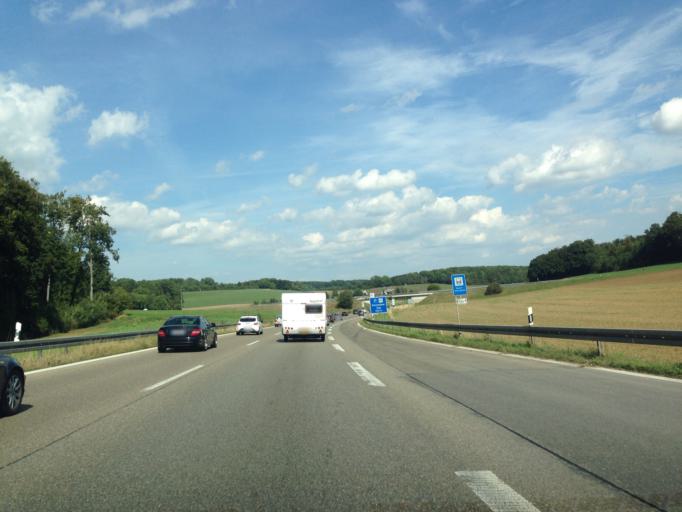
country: DE
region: Baden-Wuerttemberg
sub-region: Regierungsbezirk Stuttgart
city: Hohenstadt
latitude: 48.5469
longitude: 9.6482
